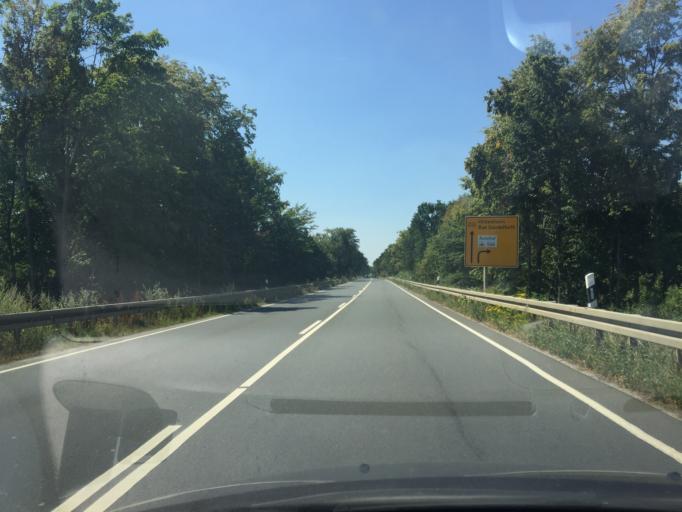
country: DE
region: Lower Saxony
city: Bockenem
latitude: 52.0013
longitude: 10.1394
